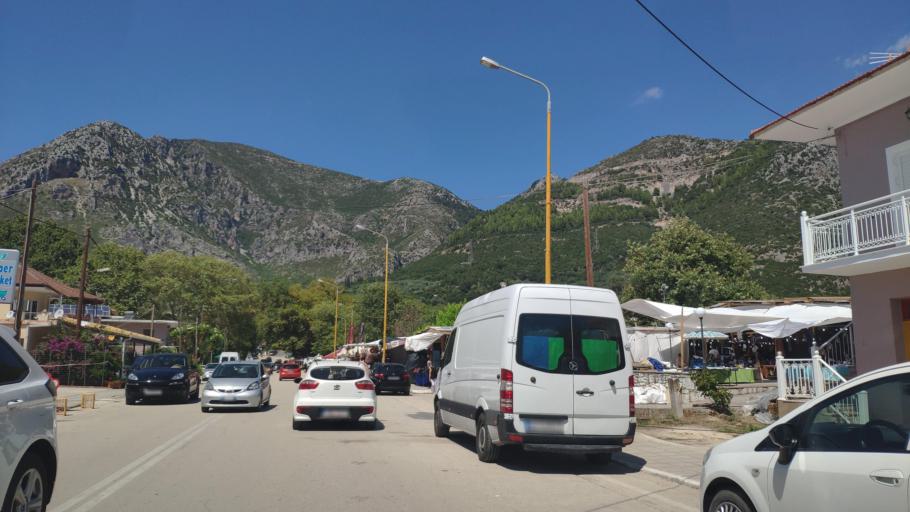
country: GR
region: Epirus
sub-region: Nomos Prevezis
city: Kanalaki
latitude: 39.3243
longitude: 20.6074
